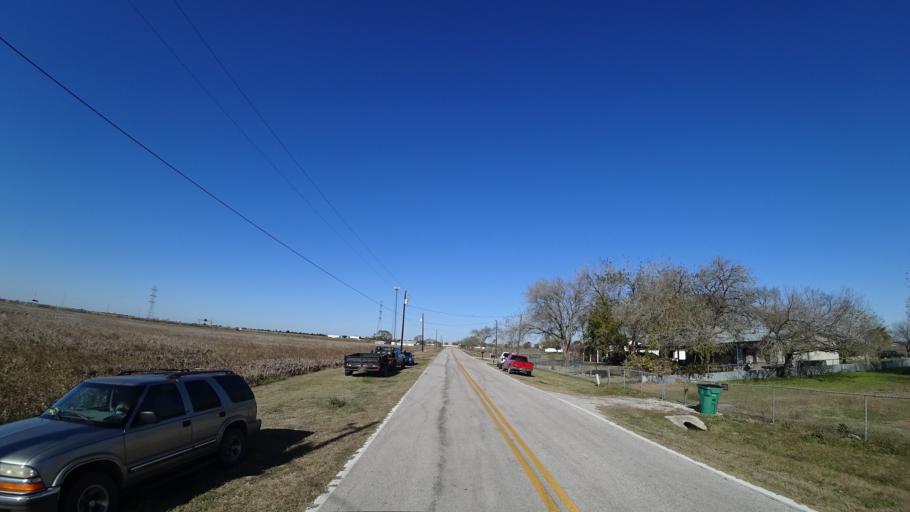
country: US
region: Texas
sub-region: Travis County
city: Onion Creek
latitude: 30.0991
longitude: -97.6649
